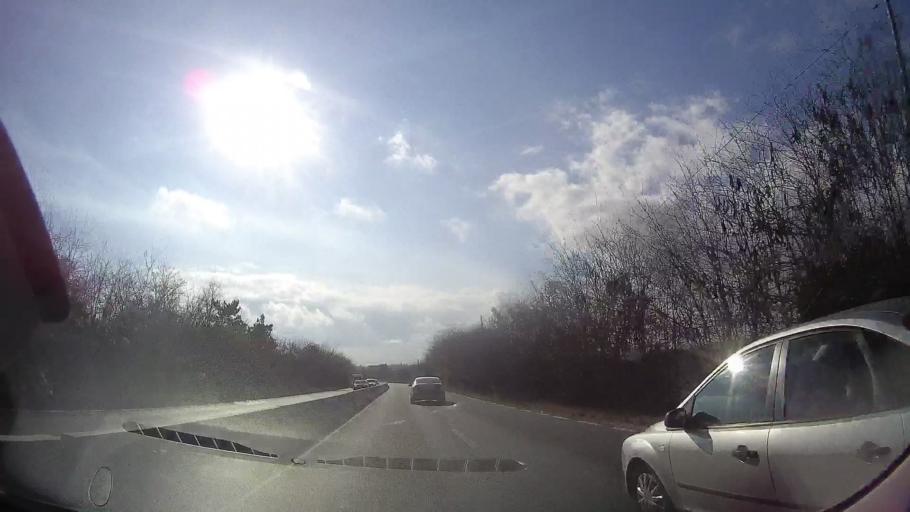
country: RO
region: Constanta
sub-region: Comuna Agigea
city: Agigea
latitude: 44.1225
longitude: 28.6131
